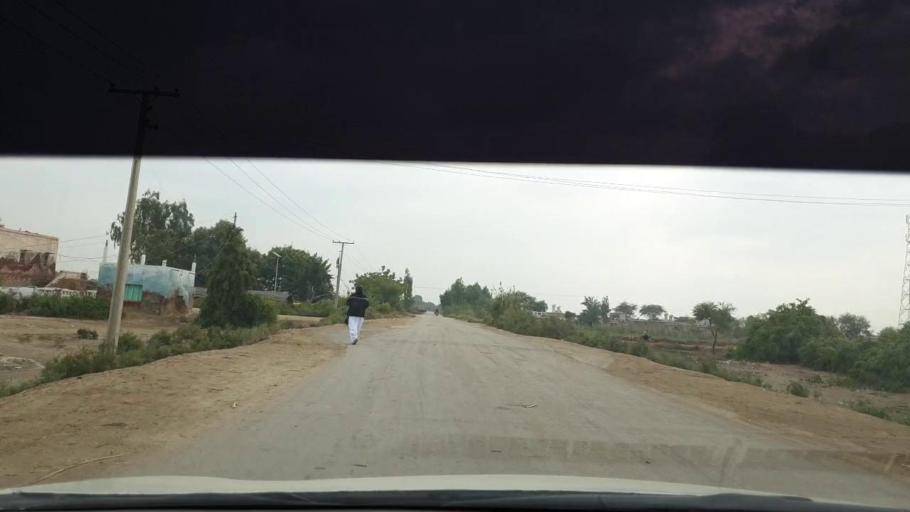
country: PK
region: Sindh
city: Berani
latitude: 25.7795
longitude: 68.8618
